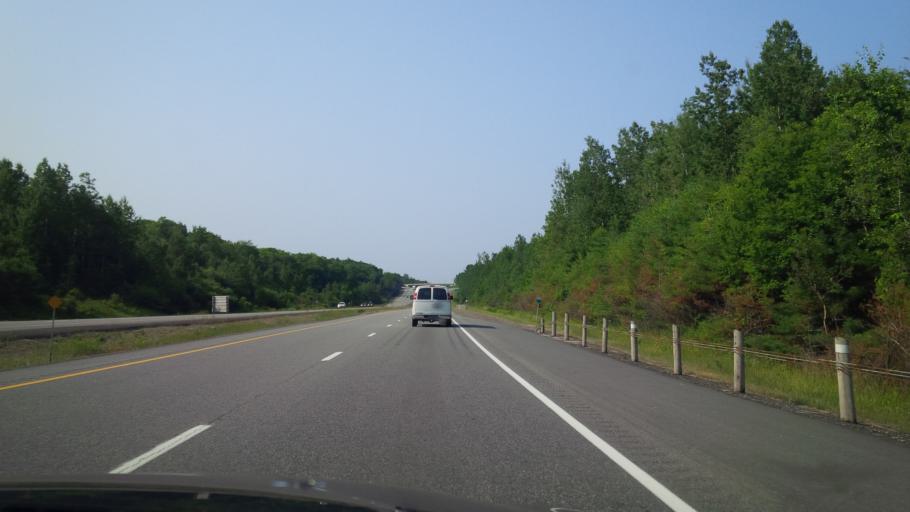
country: CA
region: Ontario
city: Bracebridge
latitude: 45.0228
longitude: -79.2929
